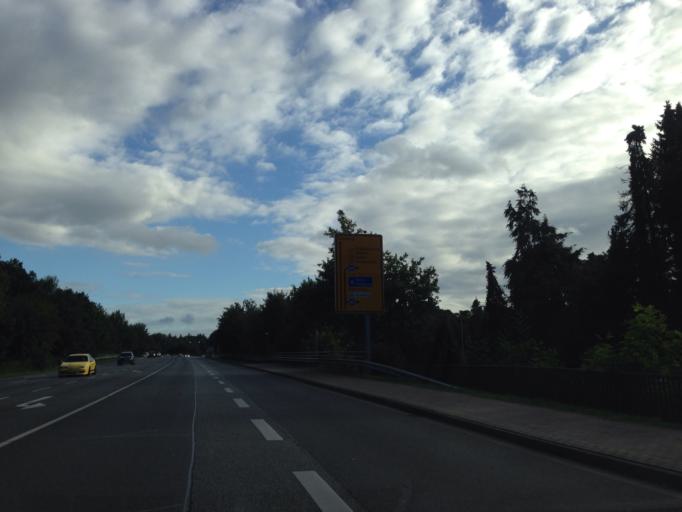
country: DE
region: Lower Saxony
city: Adendorf
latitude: 53.2713
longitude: 10.4282
